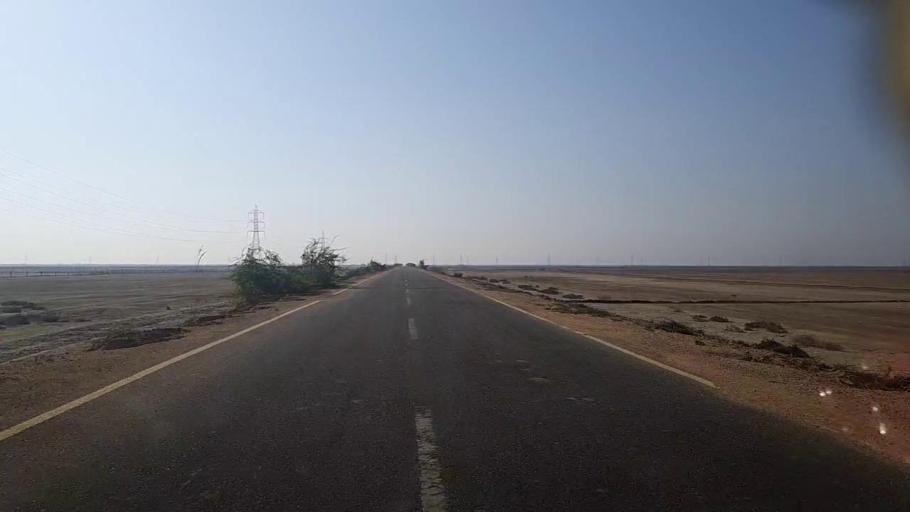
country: PK
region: Sindh
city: Mirpur Sakro
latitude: 24.6051
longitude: 67.4975
